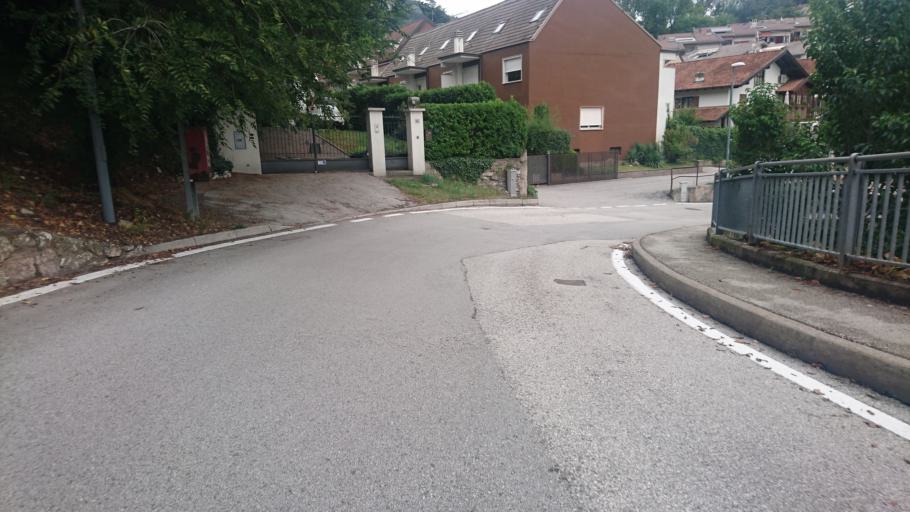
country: IT
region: Trentino-Alto Adige
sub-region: Provincia di Trento
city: Trento
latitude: 46.0727
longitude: 11.1366
